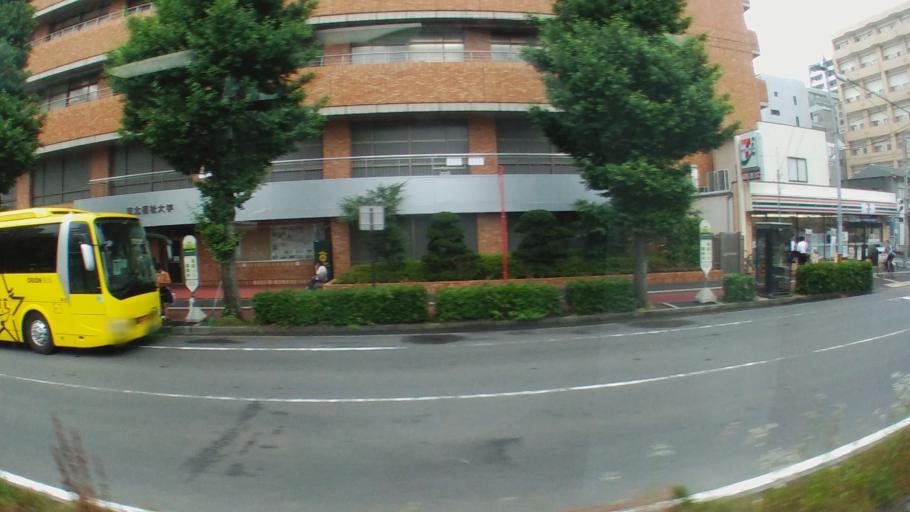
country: JP
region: Miyagi
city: Sendai-shi
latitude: 38.2599
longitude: 140.8862
